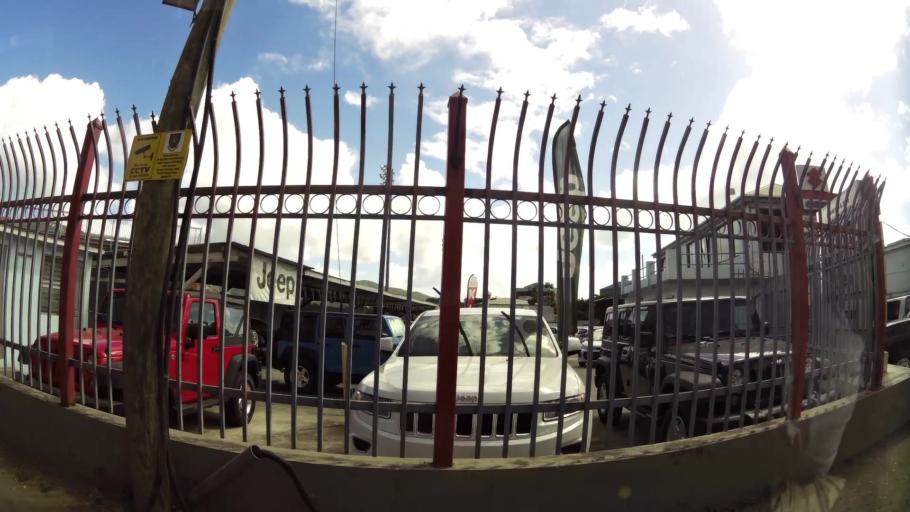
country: VG
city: Road Town
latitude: 18.4257
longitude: -64.6216
